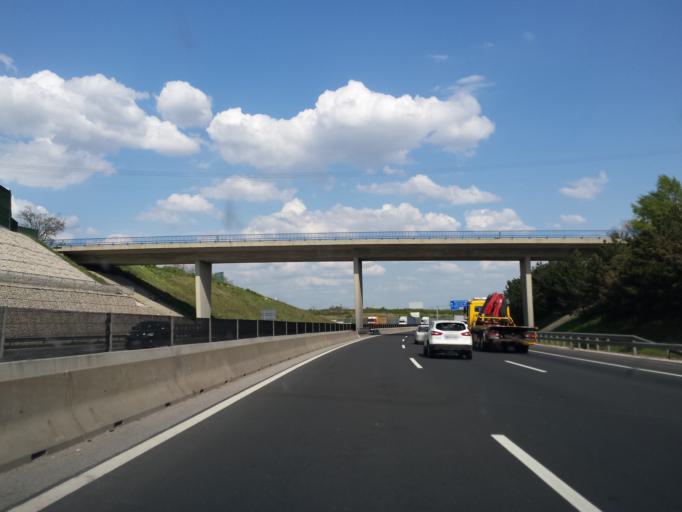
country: HU
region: Pest
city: Diosd
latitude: 47.4204
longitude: 18.9399
